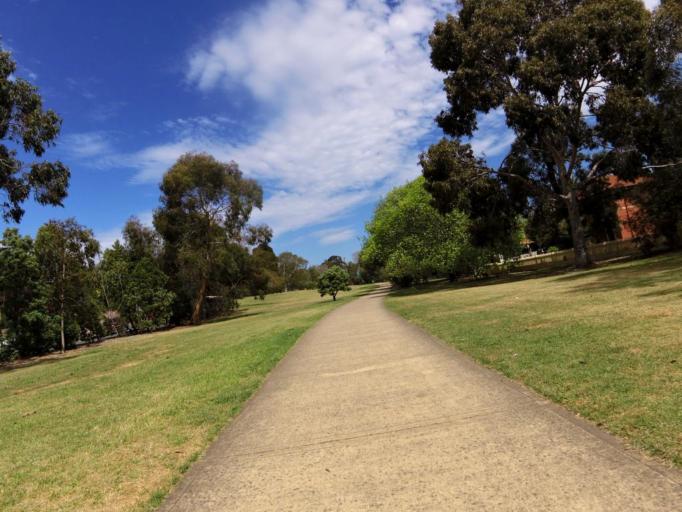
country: AU
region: Victoria
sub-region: Glen Eira
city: Murrumbeena
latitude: -37.8870
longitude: 145.0733
